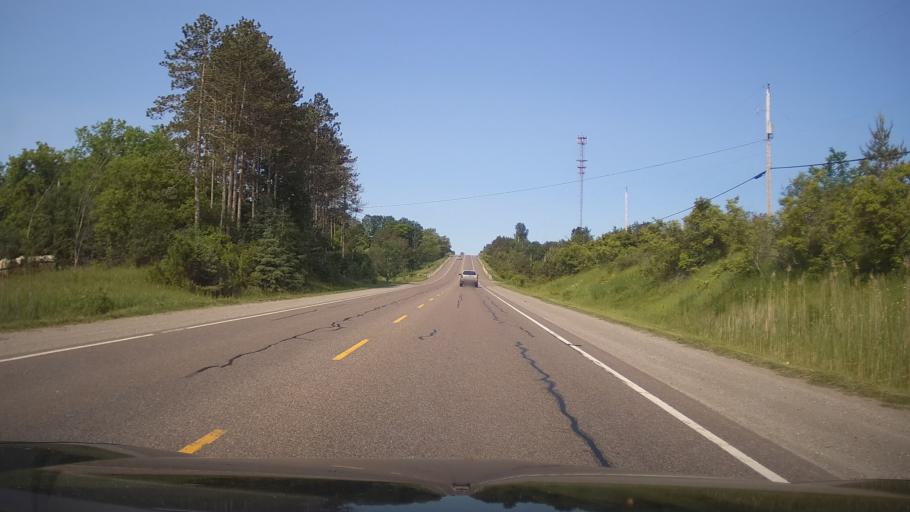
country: CA
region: Ontario
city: Omemee
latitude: 44.3179
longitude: -78.4820
